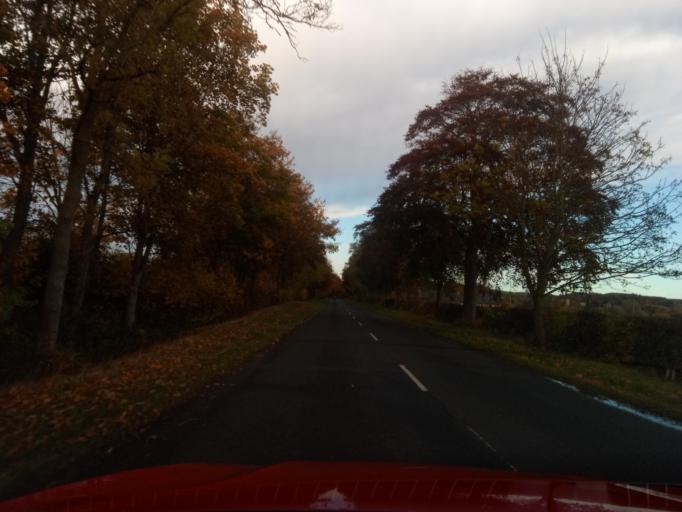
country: GB
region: England
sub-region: Northumberland
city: Ford
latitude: 55.6259
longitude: -2.1117
